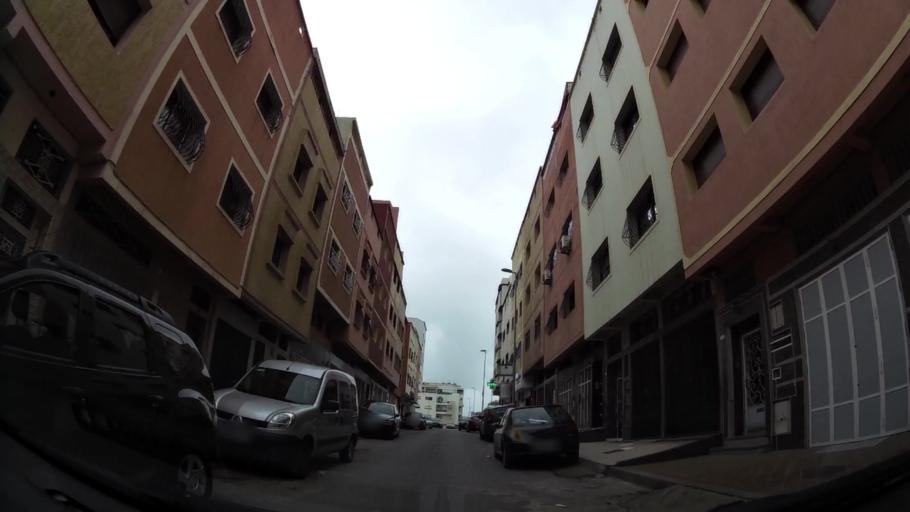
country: MA
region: Grand Casablanca
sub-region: Casablanca
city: Casablanca
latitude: 33.5311
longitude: -7.6122
